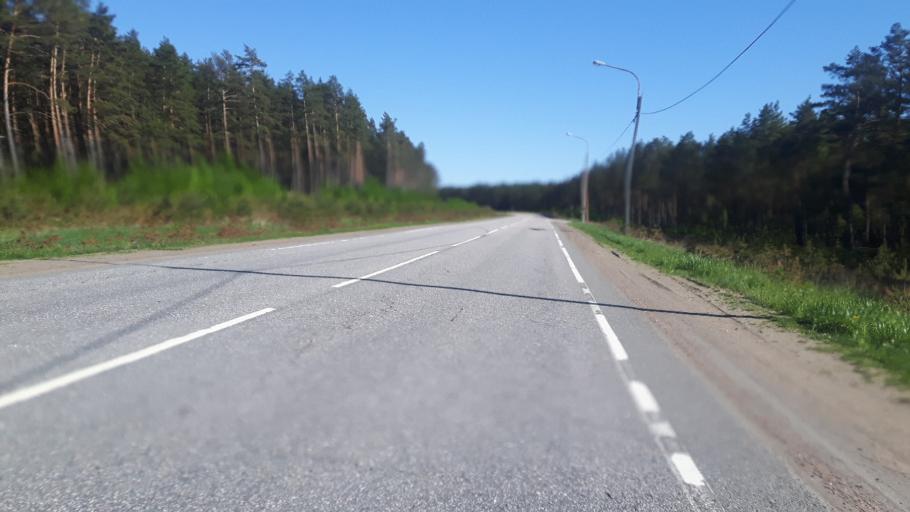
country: RU
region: Leningrad
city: Sosnovyy Bor
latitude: 60.1881
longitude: 29.0229
